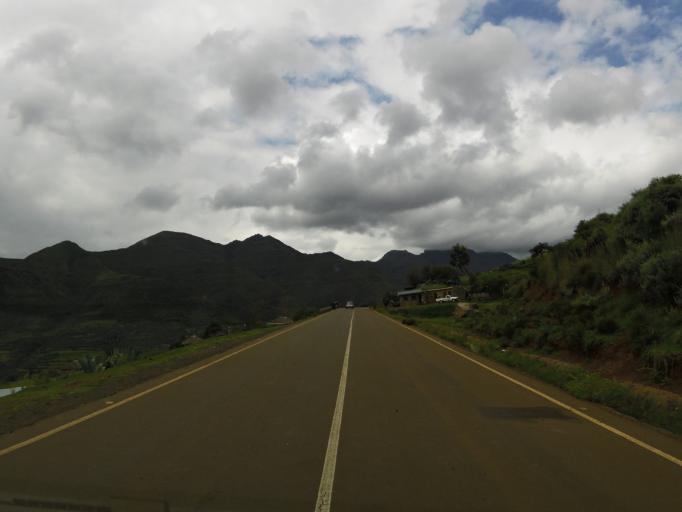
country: LS
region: Butha-Buthe
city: Butha-Buthe
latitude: -29.0447
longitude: 28.3154
